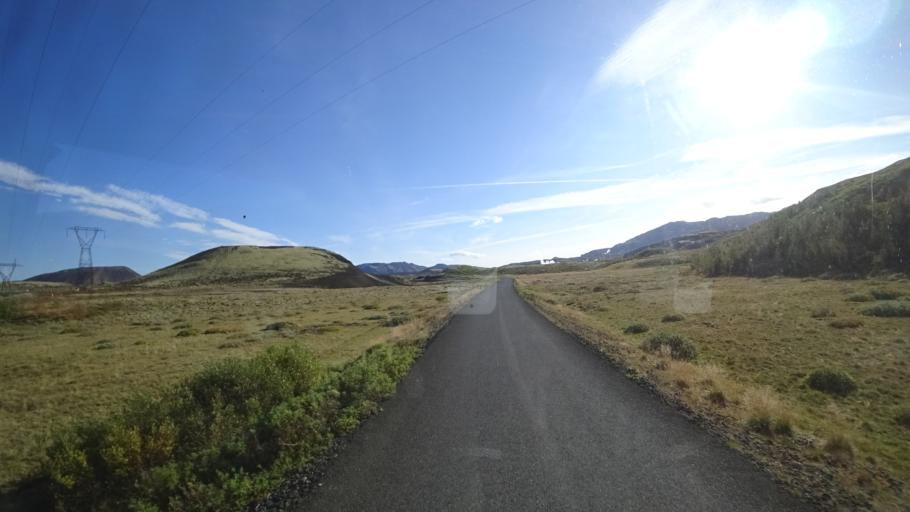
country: IS
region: South
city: Hveragerdi
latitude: 64.1283
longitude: -21.2502
